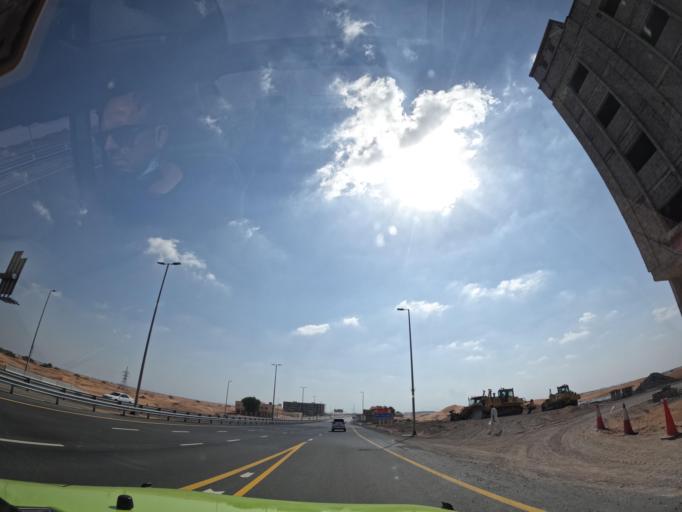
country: AE
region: Ash Shariqah
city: Adh Dhayd
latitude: 24.9408
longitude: 55.7362
